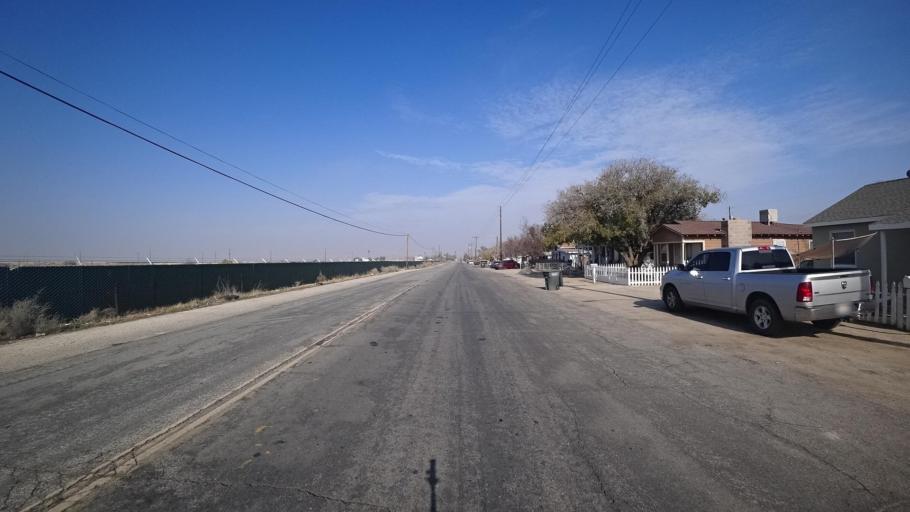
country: US
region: California
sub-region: Kern County
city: Ford City
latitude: 35.1629
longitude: -119.4652
